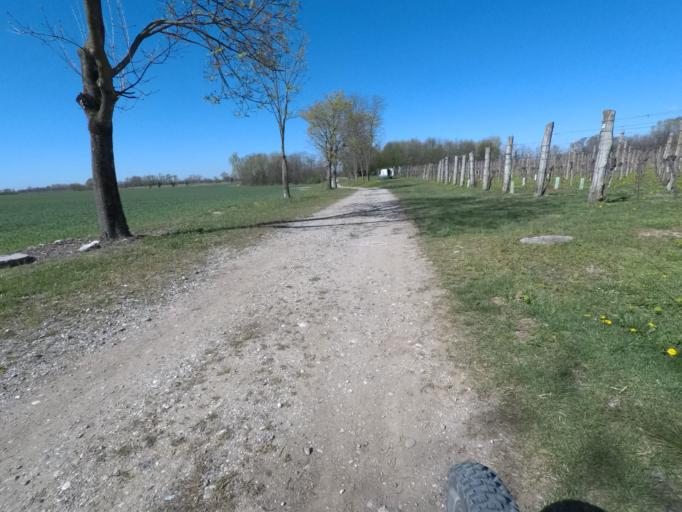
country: IT
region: Friuli Venezia Giulia
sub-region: Provincia di Udine
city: Moimacco
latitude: 46.0936
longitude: 13.3604
